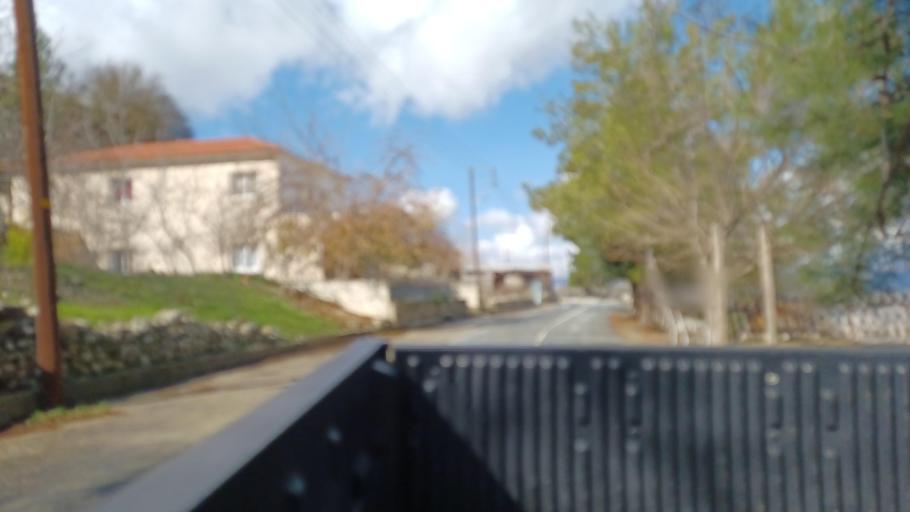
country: CY
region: Limassol
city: Pachna
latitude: 34.7793
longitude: 32.7348
